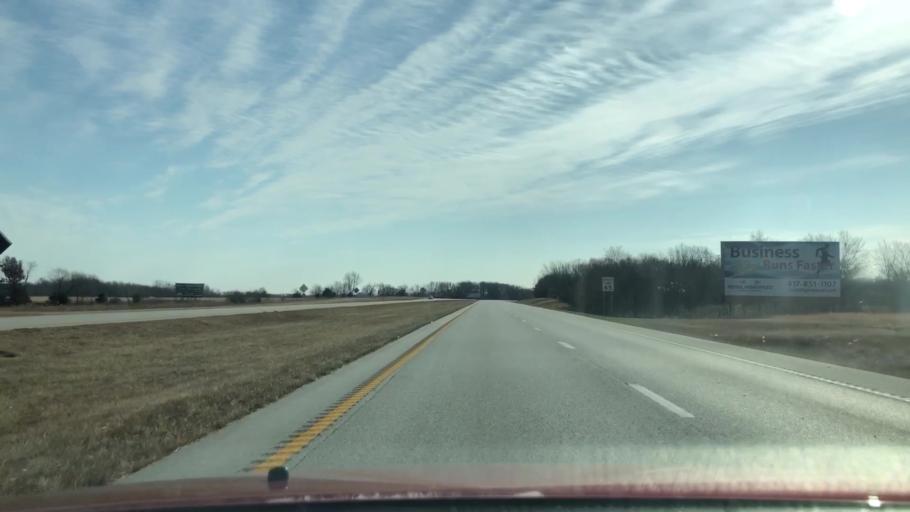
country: US
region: Missouri
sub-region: Webster County
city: Seymour
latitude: 37.1484
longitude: -92.7520
